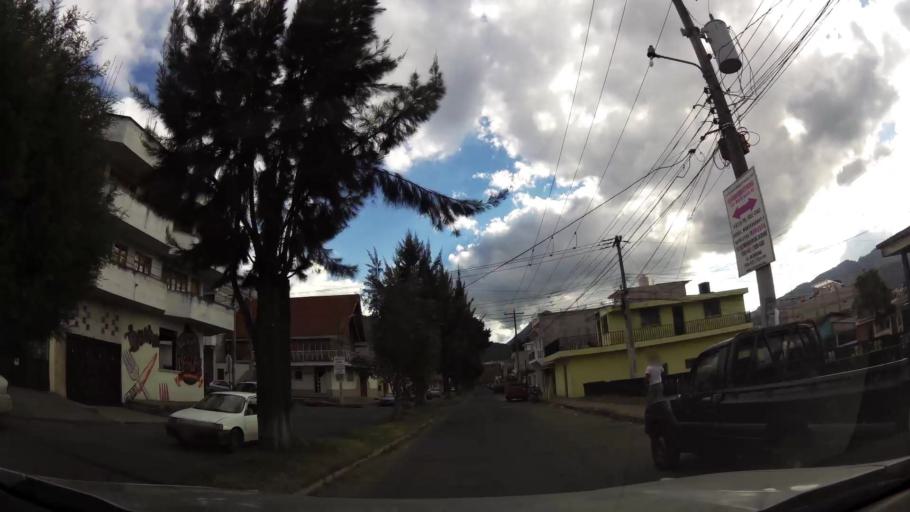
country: GT
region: Quetzaltenango
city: Quetzaltenango
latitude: 14.8424
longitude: -91.5254
